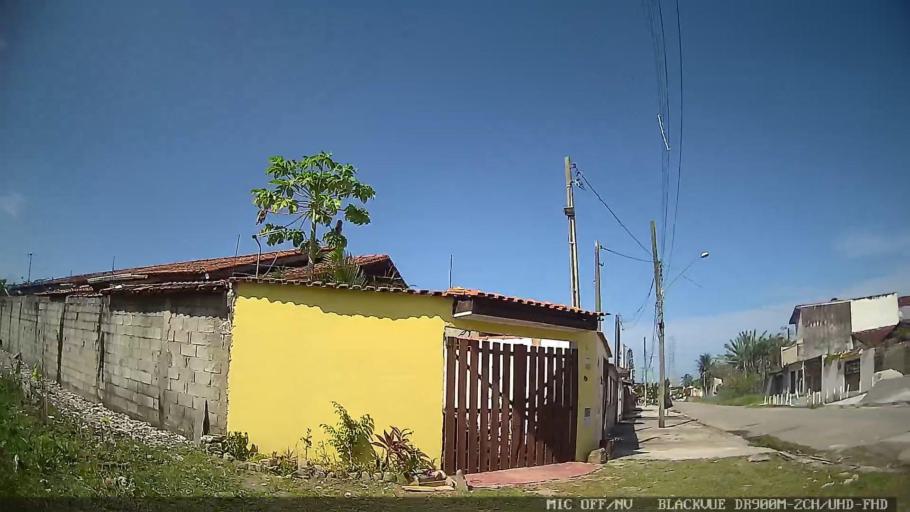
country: BR
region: Sao Paulo
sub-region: Itanhaem
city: Itanhaem
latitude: -24.1505
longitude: -46.7381
